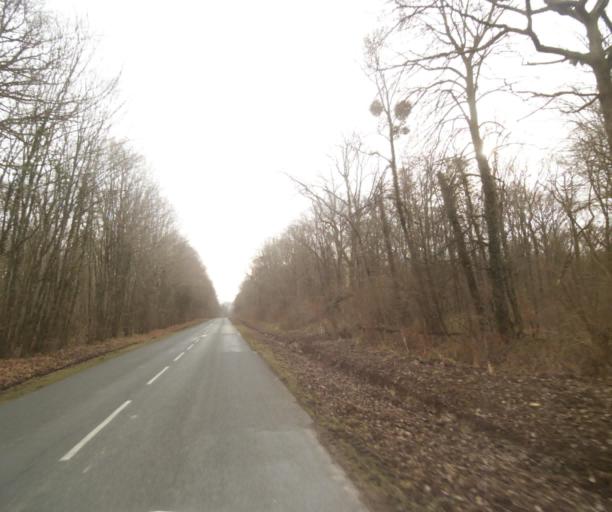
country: FR
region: Champagne-Ardenne
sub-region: Departement de la Haute-Marne
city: Villiers-en-Lieu
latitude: 48.7114
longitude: 4.8869
